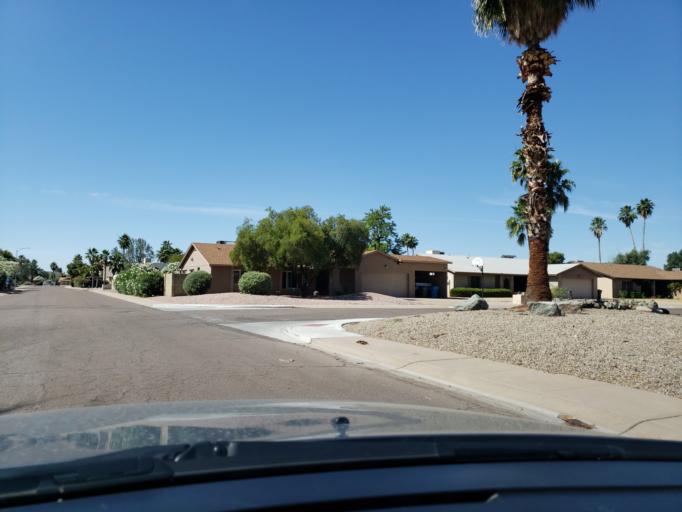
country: US
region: Arizona
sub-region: Maricopa County
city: Paradise Valley
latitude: 33.6092
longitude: -111.9757
